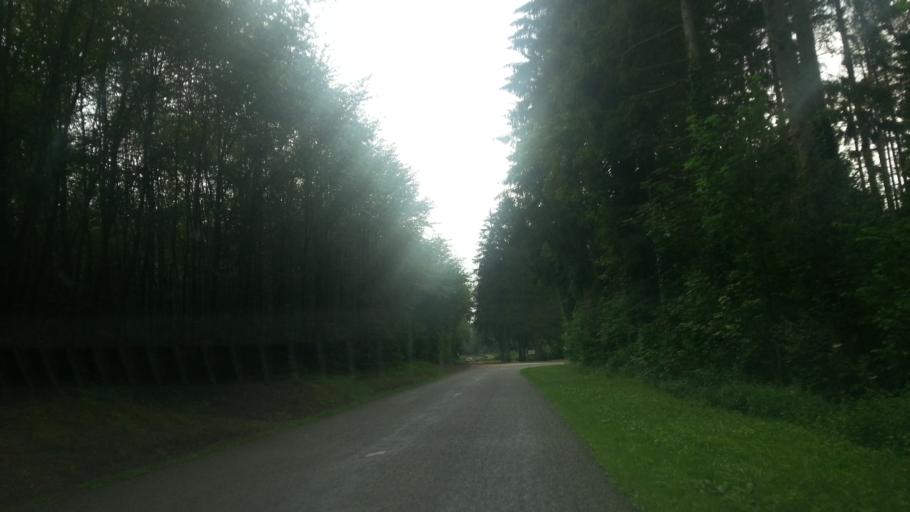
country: FR
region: Lorraine
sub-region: Departement de la Meuse
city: Belleville-sur-Meuse
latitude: 49.2209
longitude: 5.4094
